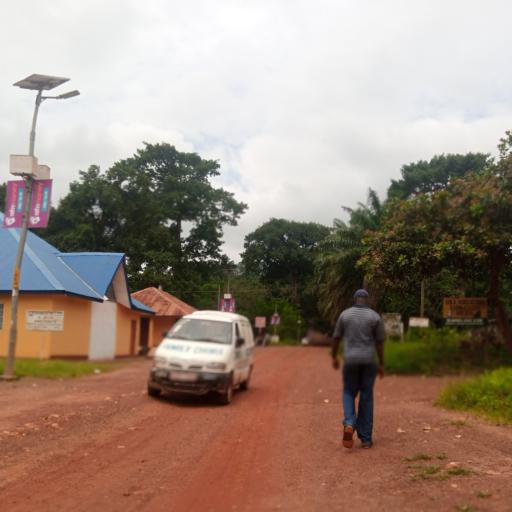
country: SL
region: Eastern Province
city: Kenema
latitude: 7.8790
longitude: -11.1956
